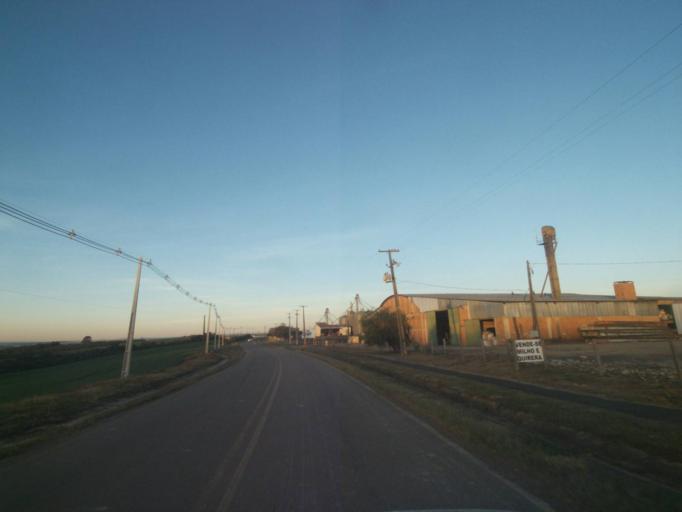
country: BR
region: Parana
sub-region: Tibagi
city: Tibagi
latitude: -24.5266
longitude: -50.4419
